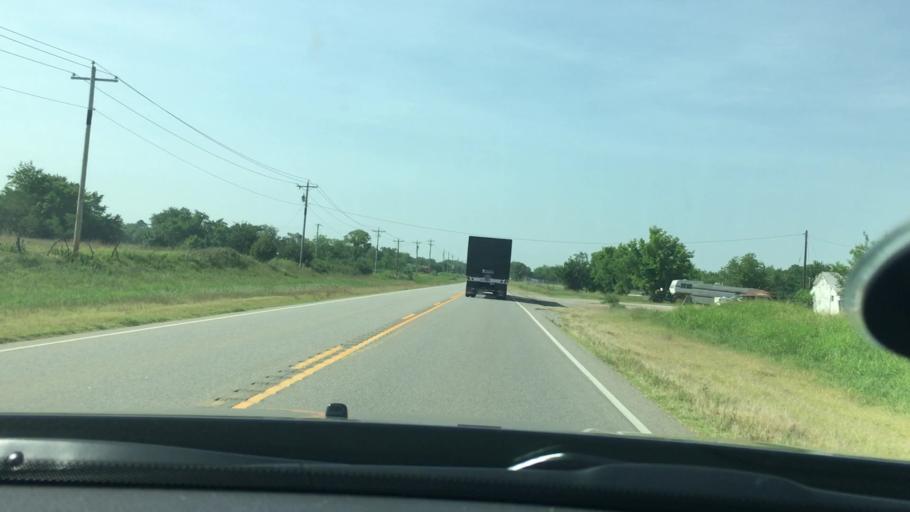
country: US
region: Oklahoma
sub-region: Coal County
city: Coalgate
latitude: 34.4818
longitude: -96.2183
